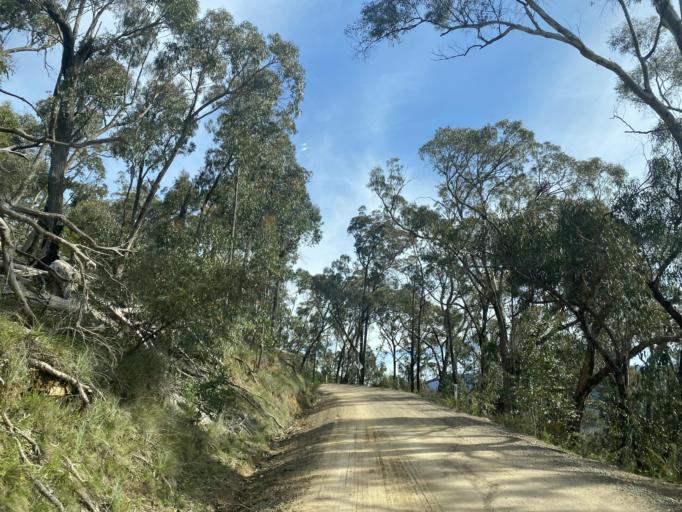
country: AU
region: Victoria
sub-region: Mansfield
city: Mansfield
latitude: -36.8382
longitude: 146.1651
